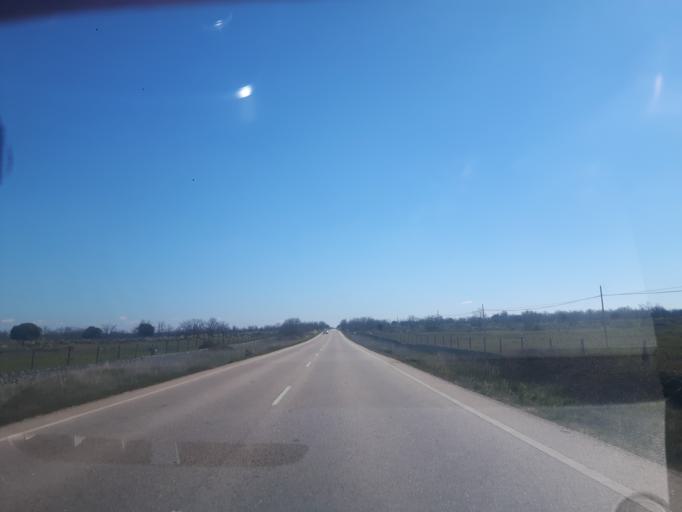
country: ES
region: Castille and Leon
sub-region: Provincia de Salamanca
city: Espadana
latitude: 41.0219
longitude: -6.2837
